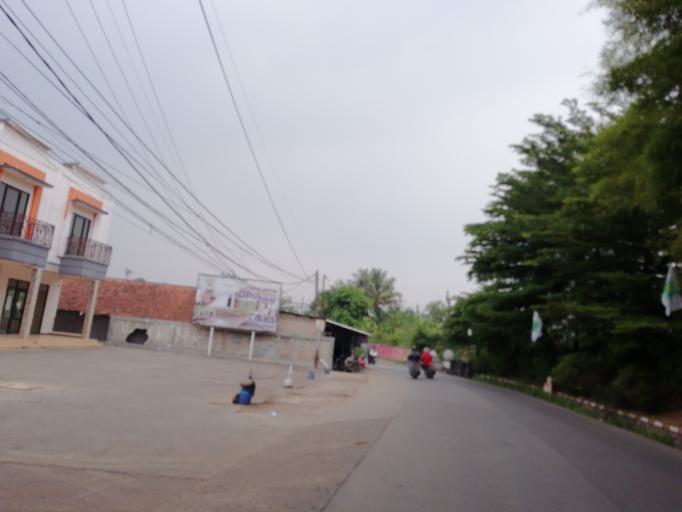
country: ID
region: West Java
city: Cibinong
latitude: -6.4716
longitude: 106.8032
